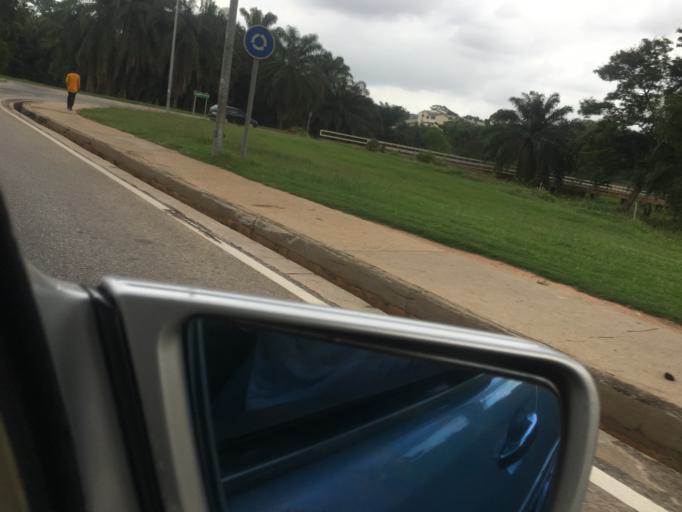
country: GH
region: Ashanti
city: Mamponteng
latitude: 6.6854
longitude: -1.5707
